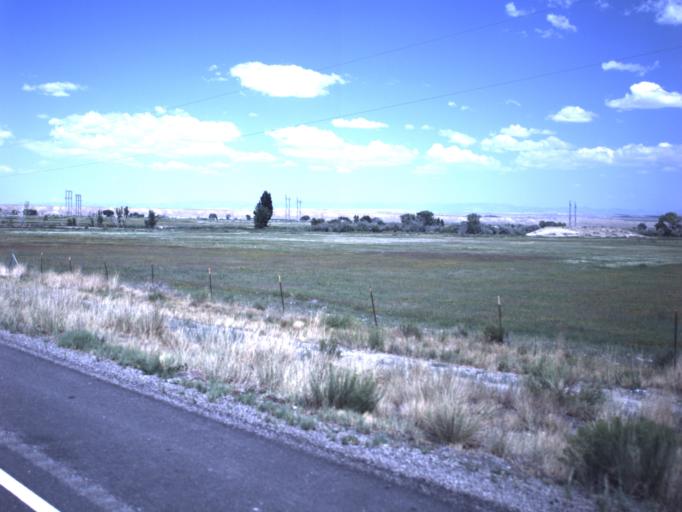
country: US
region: Utah
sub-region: Emery County
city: Castle Dale
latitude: 39.2508
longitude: -110.9863
